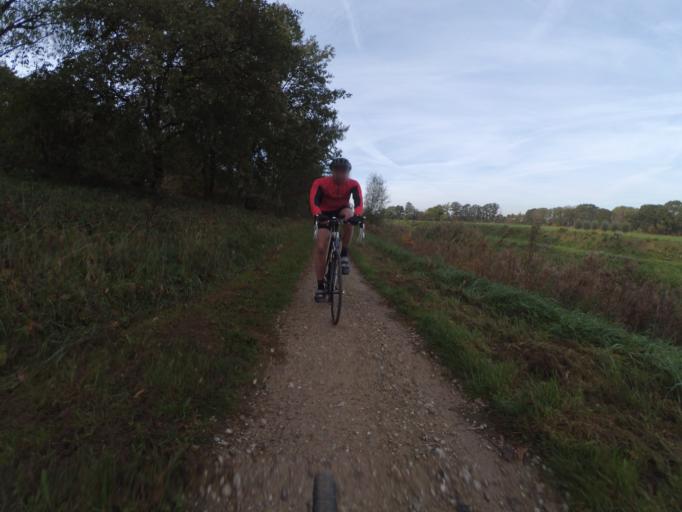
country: NL
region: Gelderland
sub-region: Gemeente Lochem
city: Epse
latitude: 52.2393
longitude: 6.2385
